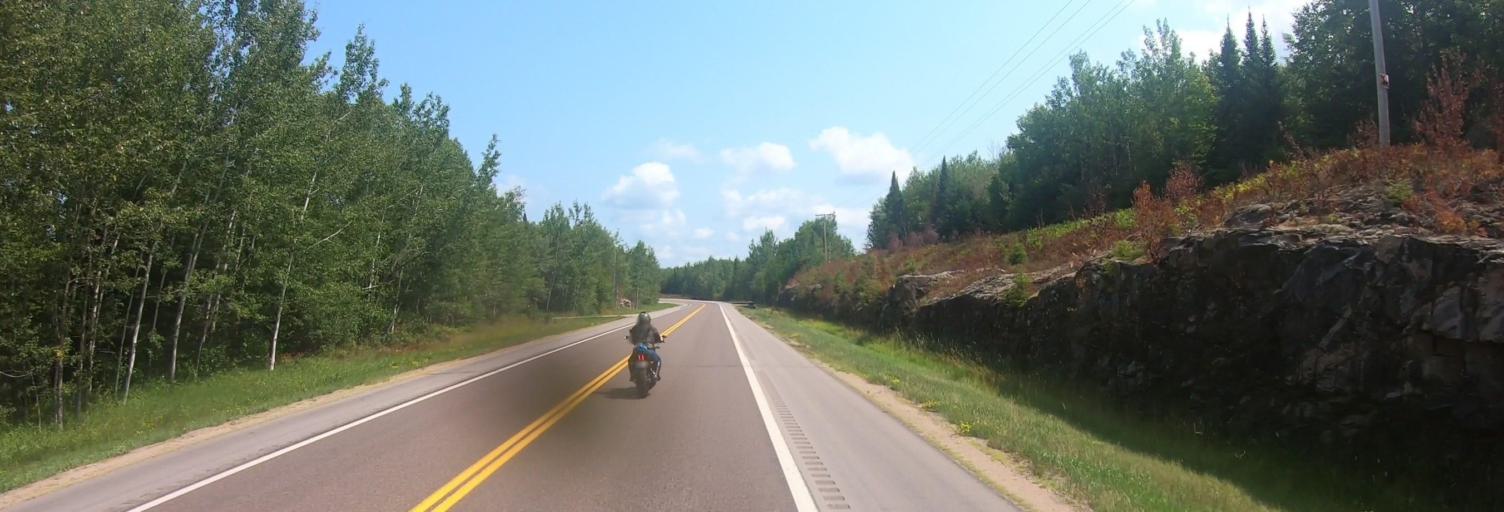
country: US
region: Minnesota
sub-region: Saint Louis County
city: Mountain Iron
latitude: 48.0690
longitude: -92.6945
